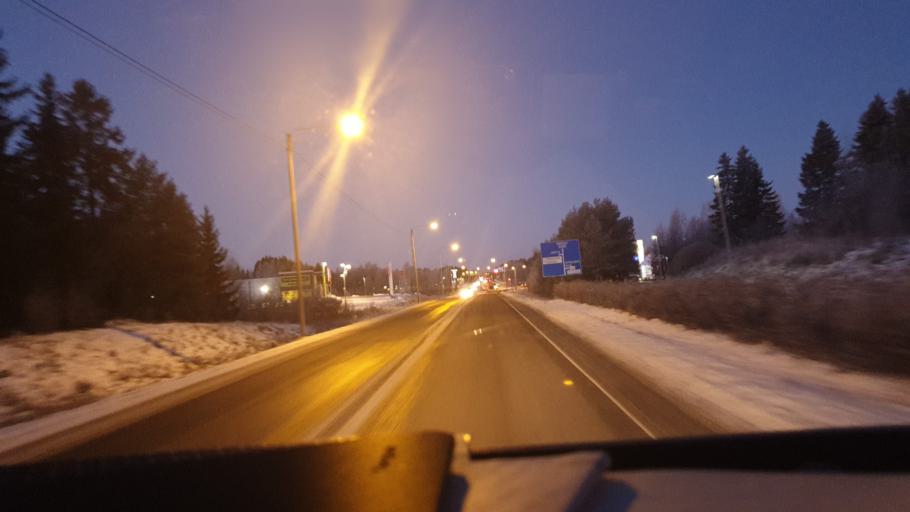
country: FI
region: Northern Ostrobothnia
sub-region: Raahe
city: Raahe
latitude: 64.6869
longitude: 24.5758
